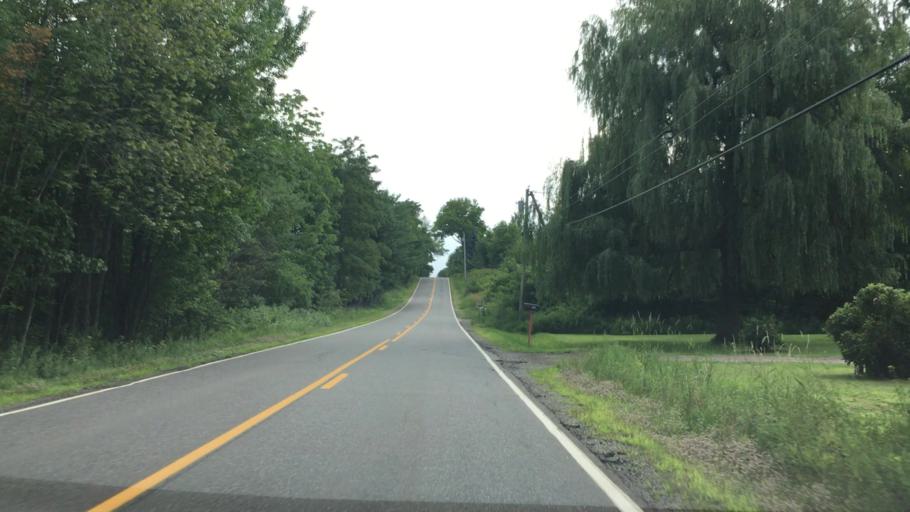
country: US
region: Maine
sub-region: Waldo County
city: Belfast
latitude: 44.3691
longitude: -69.0374
